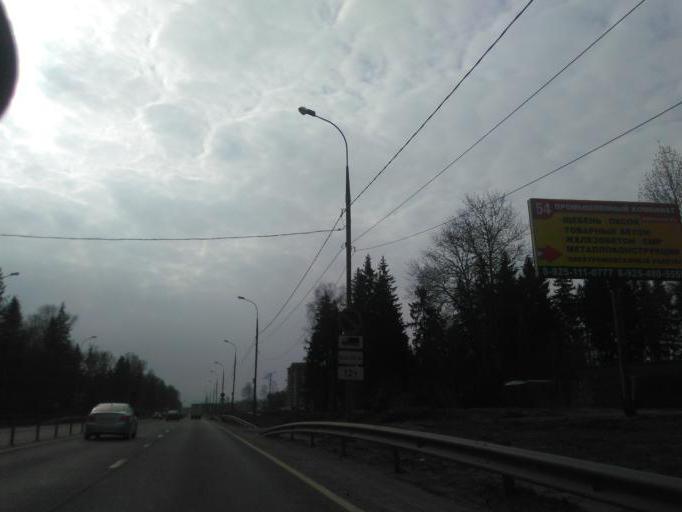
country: RU
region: Moskovskaya
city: Yermolino
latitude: 56.1357
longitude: 37.4999
